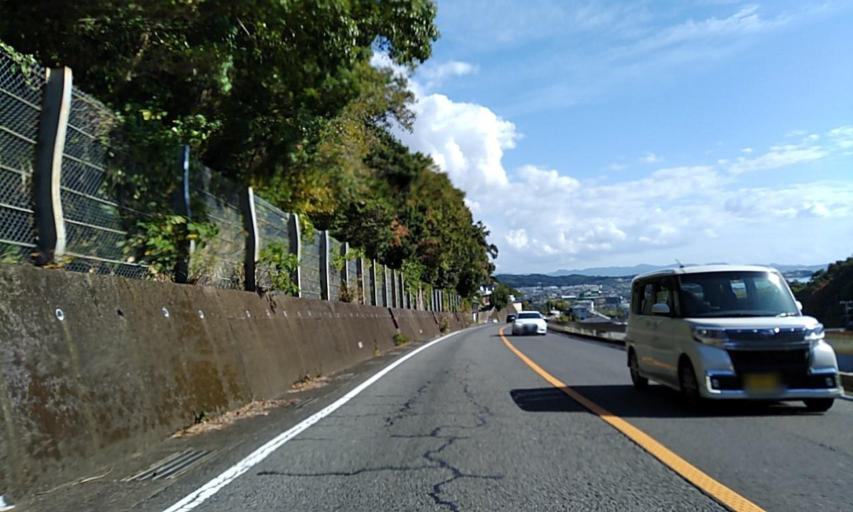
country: JP
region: Wakayama
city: Tanabe
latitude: 33.7785
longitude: 135.3075
